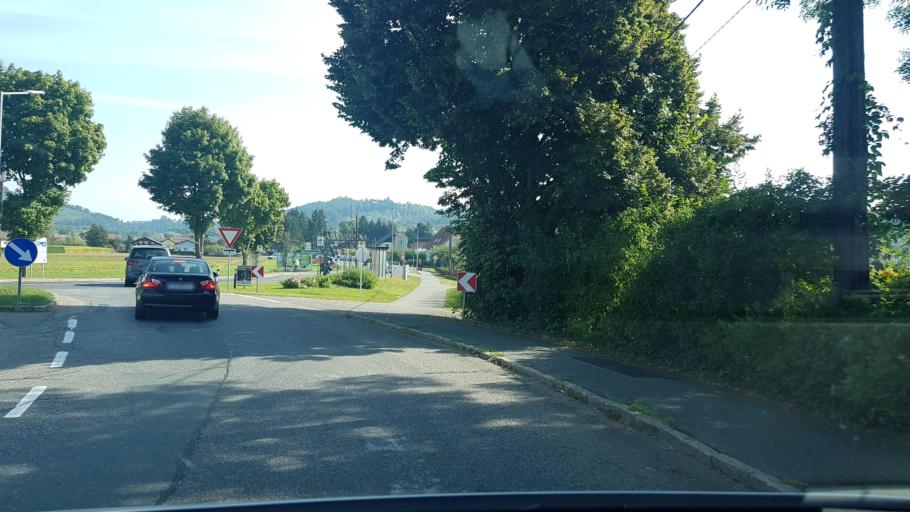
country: AT
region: Styria
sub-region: Politischer Bezirk Leibnitz
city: Heimschuh
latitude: 46.7641
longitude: 15.4948
